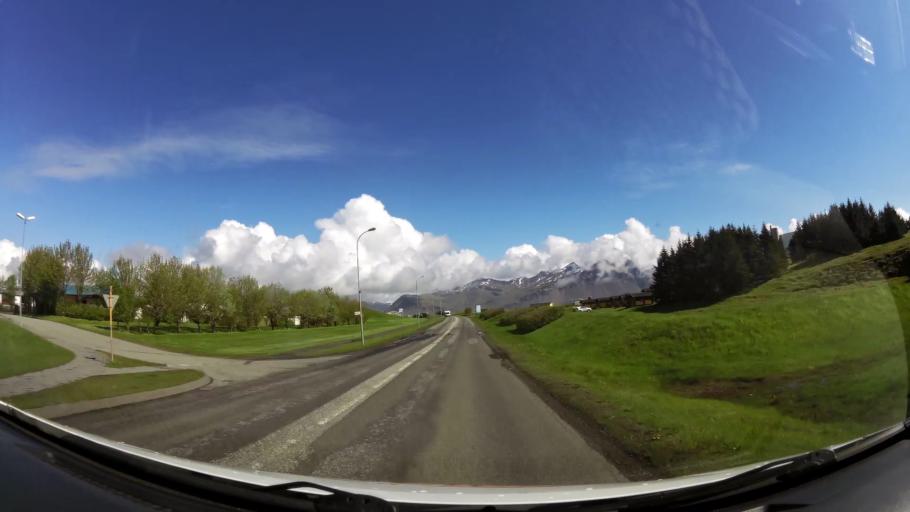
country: IS
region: East
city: Hoefn
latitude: 64.2566
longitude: -15.2069
